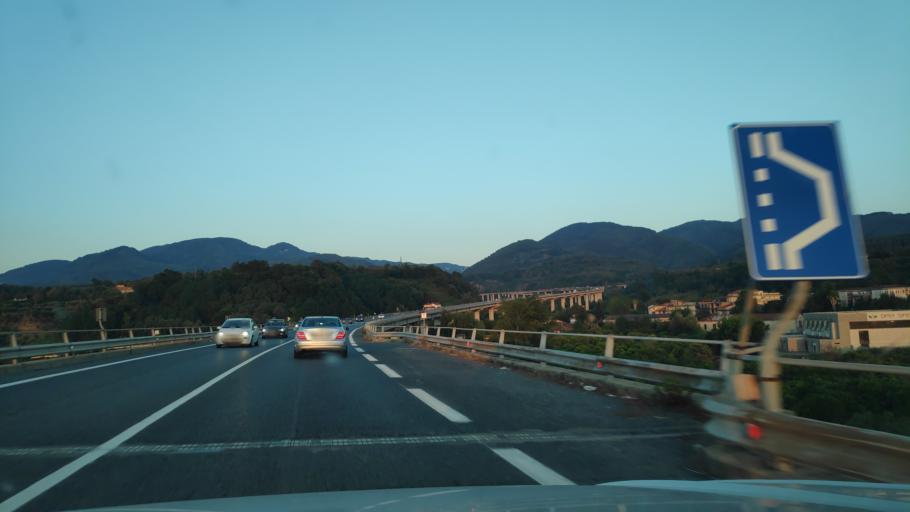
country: IT
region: Calabria
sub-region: Provincia di Reggio Calabria
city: Anoia Superiore
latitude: 38.4217
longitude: 16.0945
